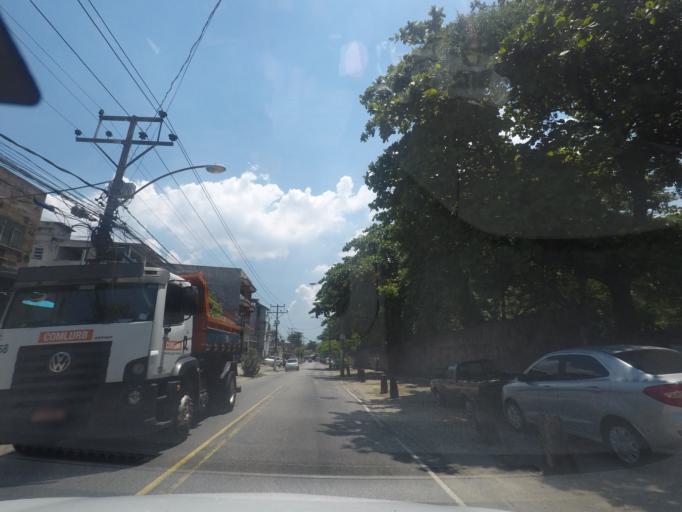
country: BR
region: Rio de Janeiro
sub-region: Duque De Caxias
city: Duque de Caxias
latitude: -22.8195
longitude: -43.3050
